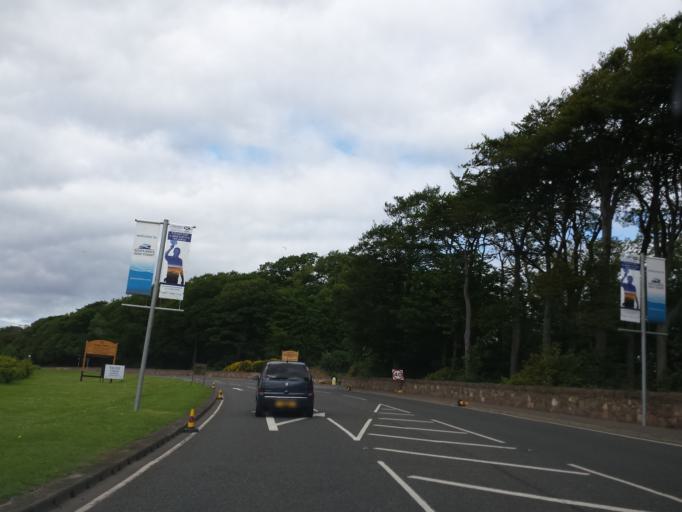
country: GB
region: Scotland
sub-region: East Lothian
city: Gullane
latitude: 56.0415
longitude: -2.7945
